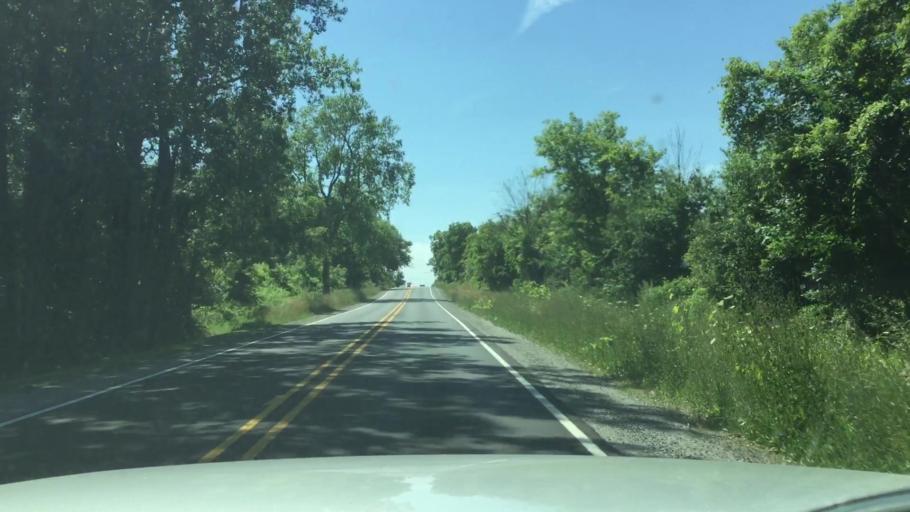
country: US
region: Michigan
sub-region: Genesee County
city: Flint
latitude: 43.0069
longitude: -83.7650
